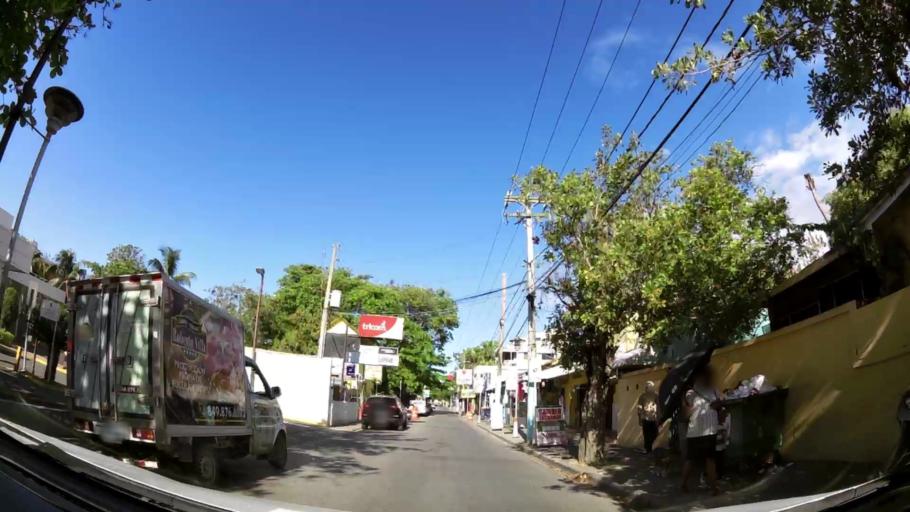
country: DO
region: Santo Domingo
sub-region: Santo Domingo
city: Boca Chica
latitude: 18.4480
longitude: -69.6101
